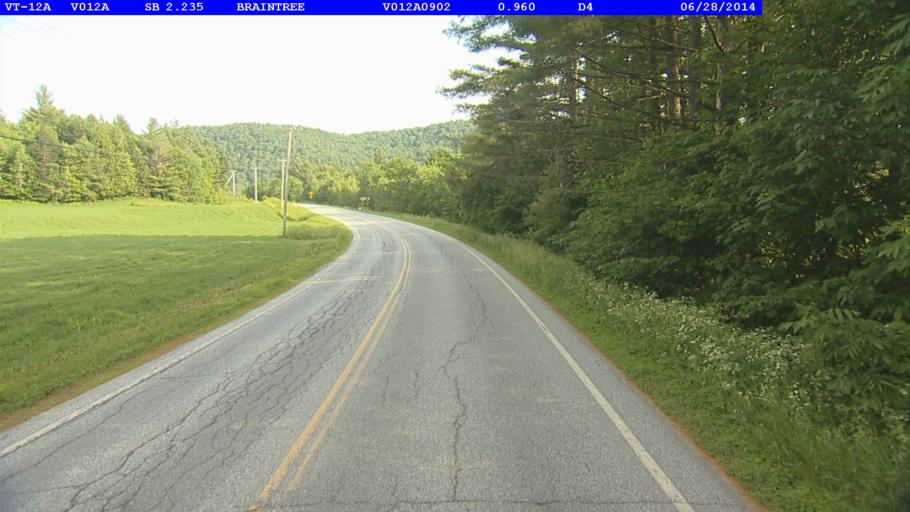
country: US
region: Vermont
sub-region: Orange County
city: Randolph
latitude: 43.9363
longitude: -72.7038
